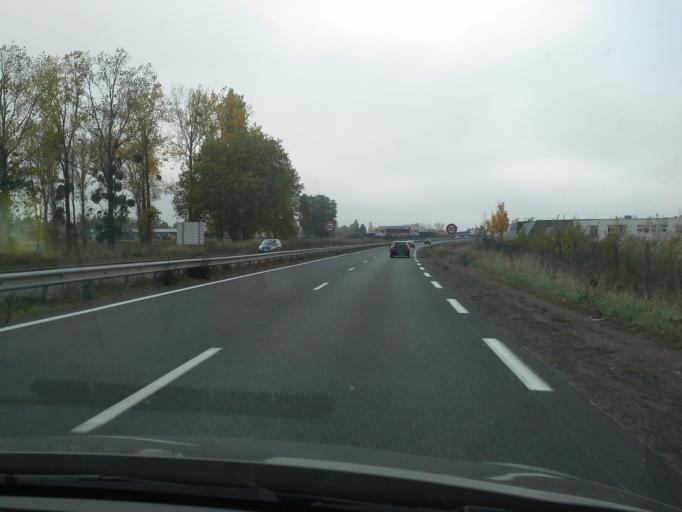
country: FR
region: Centre
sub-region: Departement d'Indre-et-Loire
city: Parcay-Meslay
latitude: 47.4417
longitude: 0.7189
